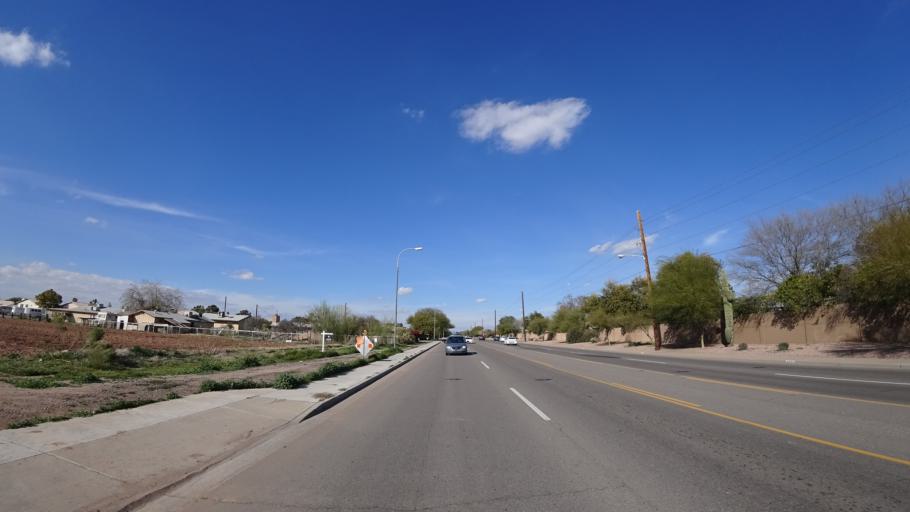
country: US
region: Arizona
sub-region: Maricopa County
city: Peoria
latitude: 33.5987
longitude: -112.2203
